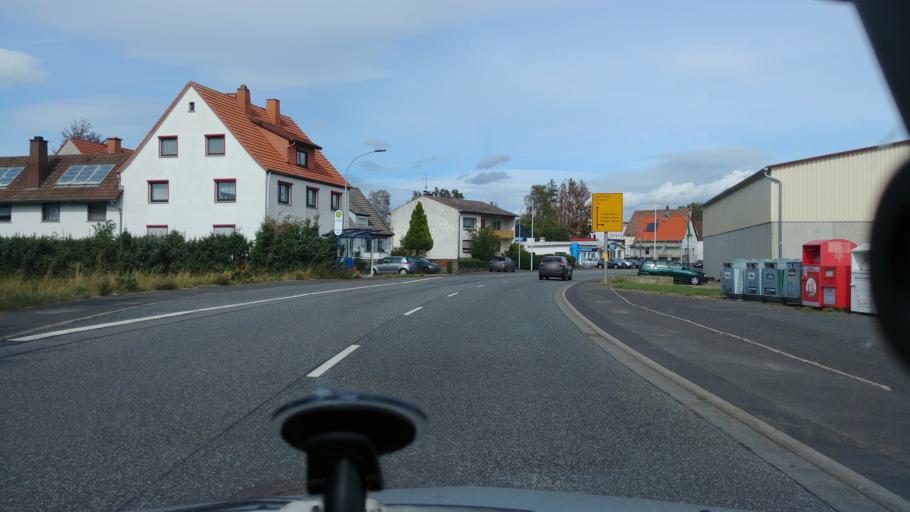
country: DE
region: Hesse
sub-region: Regierungsbezirk Giessen
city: Grebenhain
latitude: 50.4930
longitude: 9.3462
